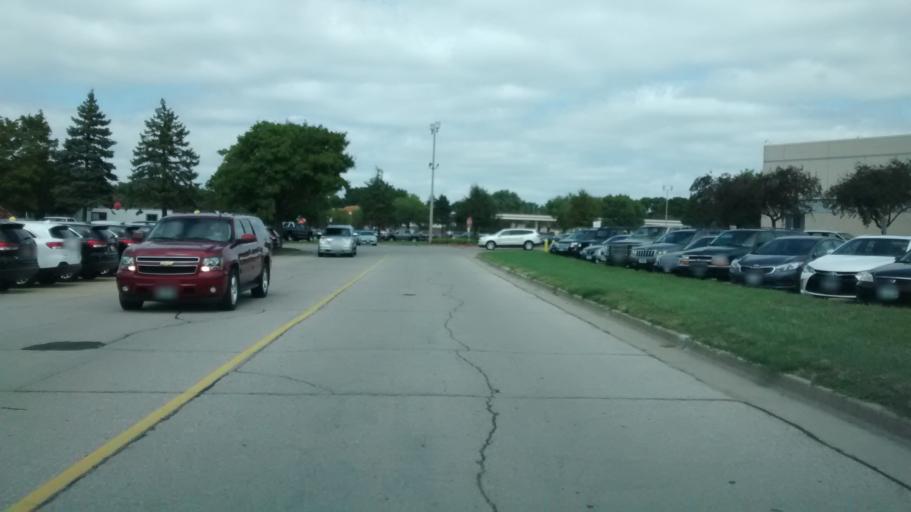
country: US
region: Iowa
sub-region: Woodbury County
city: Sergeant Bluff
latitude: 42.4455
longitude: -96.3489
